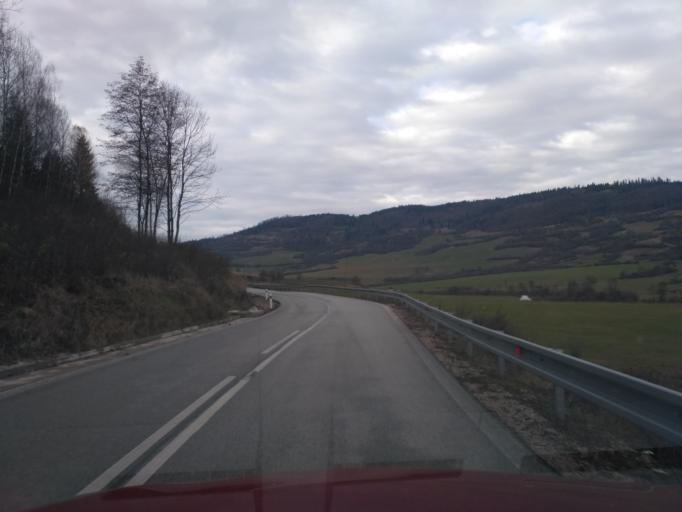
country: SK
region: Kosicky
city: Spisska Nova Ves
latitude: 48.8305
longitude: 20.6498
